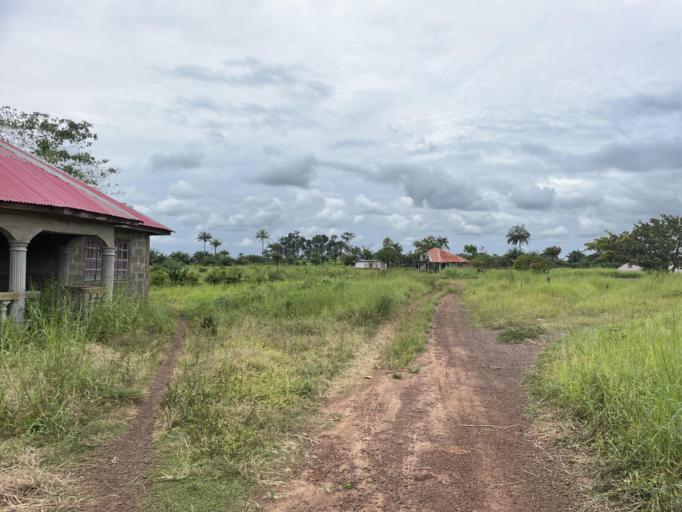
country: SL
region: Northern Province
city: Kambia
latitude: 9.1327
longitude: -12.9079
